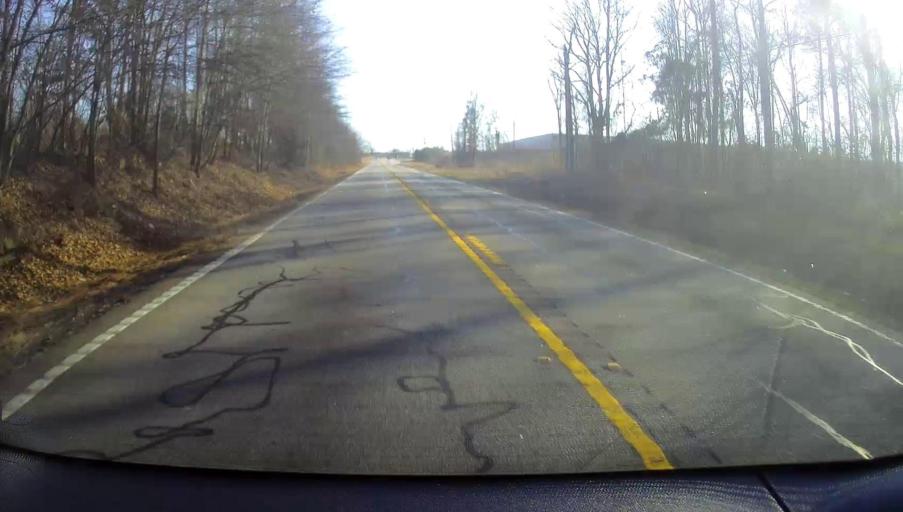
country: US
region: Georgia
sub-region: Henry County
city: McDonough
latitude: 33.3789
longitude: -84.1787
